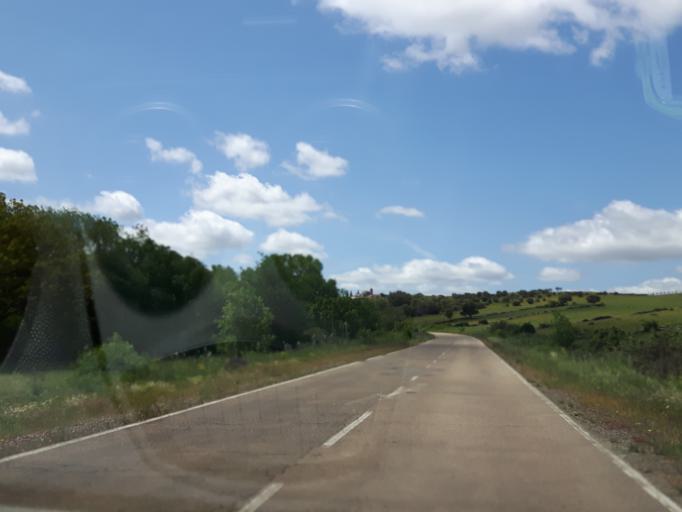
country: ES
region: Castille and Leon
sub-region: Provincia de Salamanca
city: Aldea del Obispo
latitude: 40.7178
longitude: -6.7831
